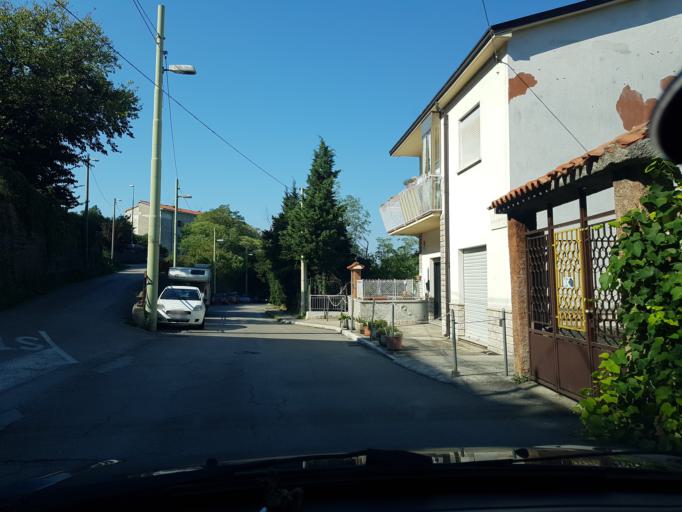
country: IT
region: Friuli Venezia Giulia
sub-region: Provincia di Trieste
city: Trieste
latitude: 45.6259
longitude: 13.8017
